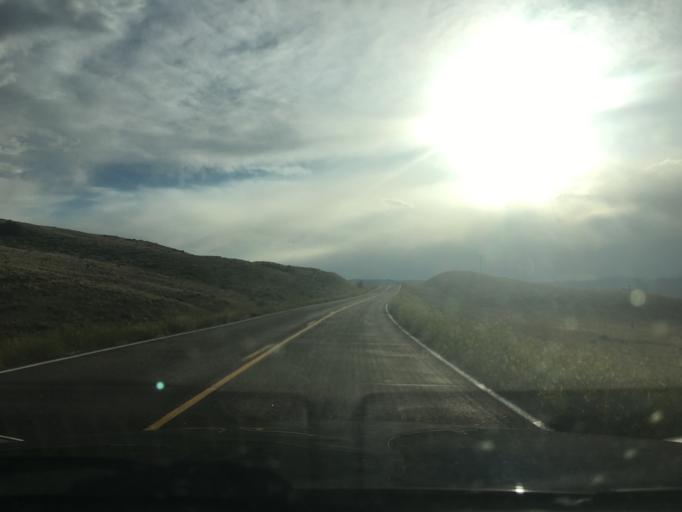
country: US
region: Wyoming
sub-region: Albany County
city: Laramie
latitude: 41.2861
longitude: -106.0439
